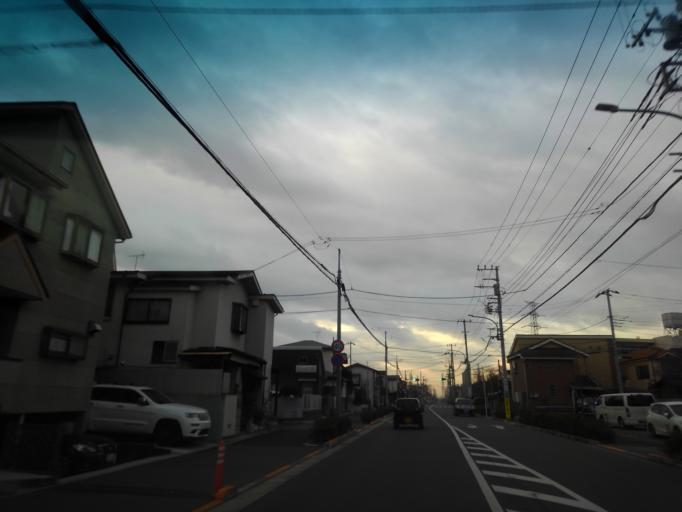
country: JP
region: Tokyo
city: Higashimurayama-shi
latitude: 35.7302
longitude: 139.4441
